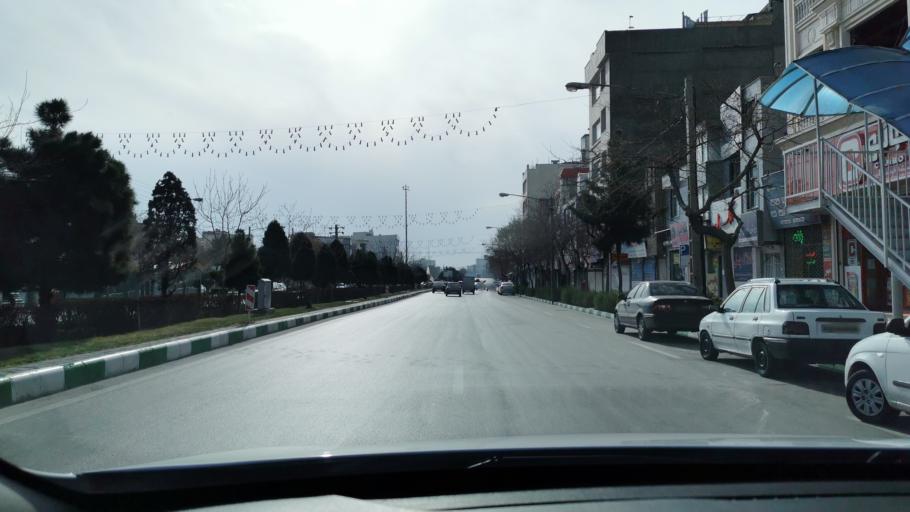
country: IR
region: Razavi Khorasan
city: Mashhad
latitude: 36.2969
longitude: 59.5278
